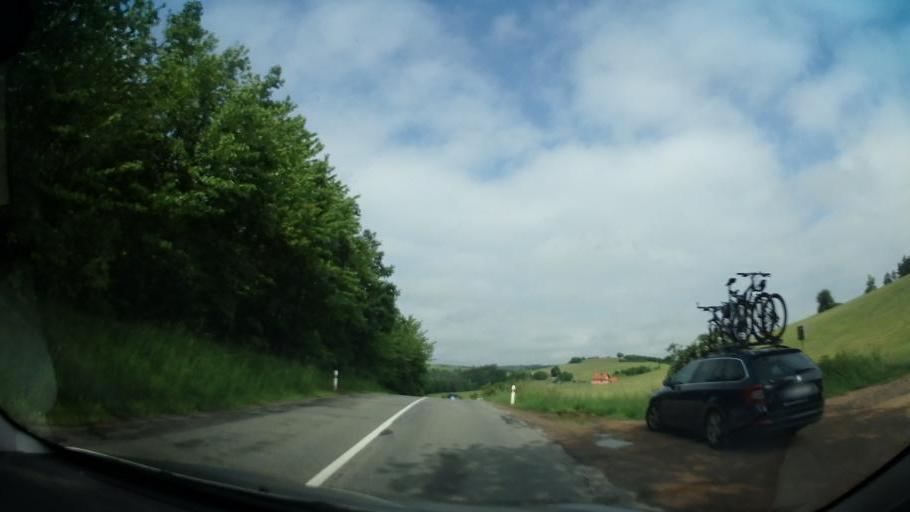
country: CZ
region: South Moravian
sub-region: Okres Brno-Venkov
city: Dolni Loucky
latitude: 49.3705
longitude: 16.3692
